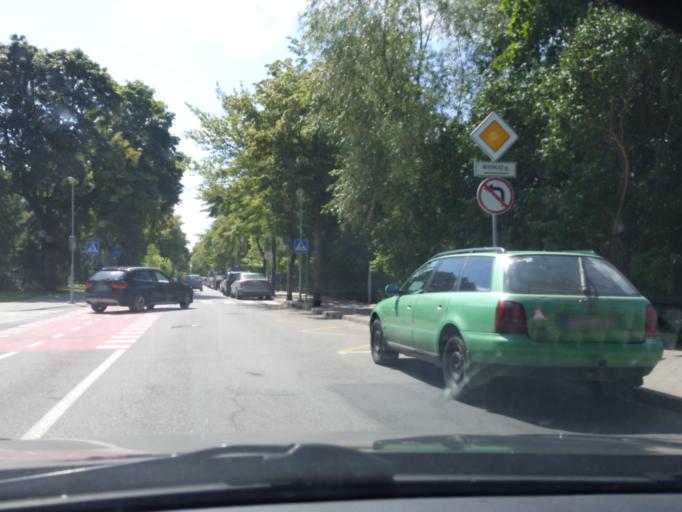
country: LT
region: Klaipedos apskritis
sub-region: Klaipeda
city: Palanga
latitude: 55.9269
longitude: 21.0719
